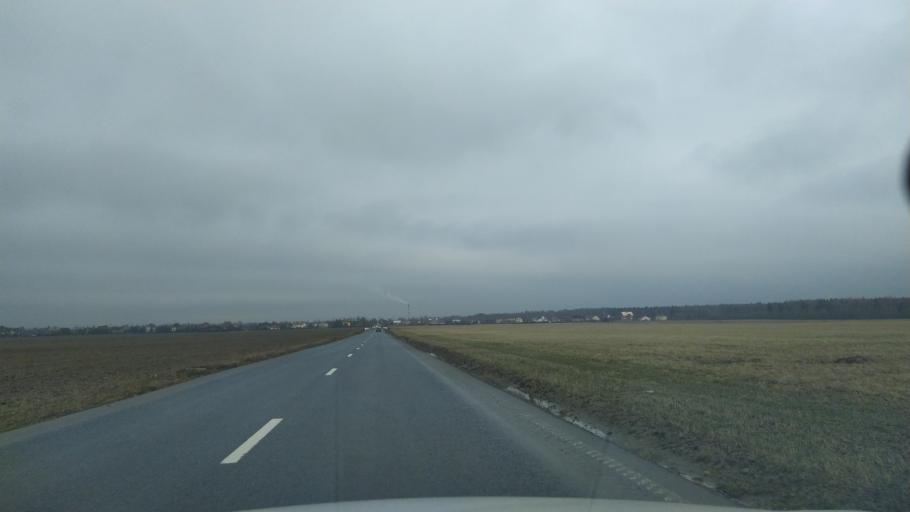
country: RU
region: St.-Petersburg
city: Aleksandrovskaya
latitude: 59.7156
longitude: 30.3362
